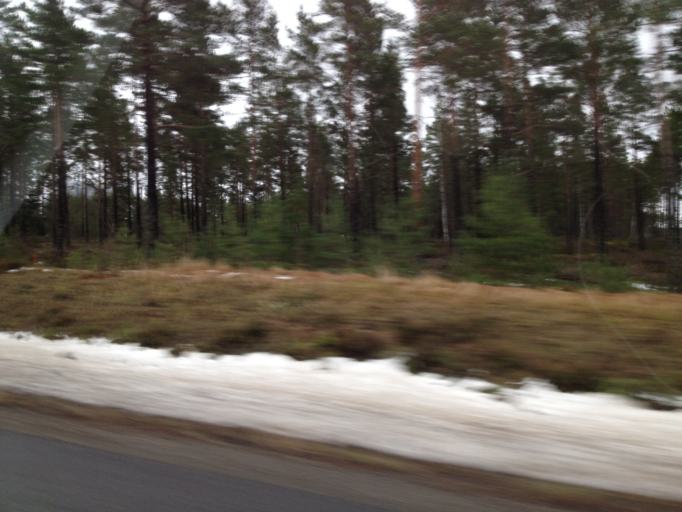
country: FI
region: Uusimaa
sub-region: Raaseporin
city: Hanko
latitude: 59.8545
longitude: 23.0149
